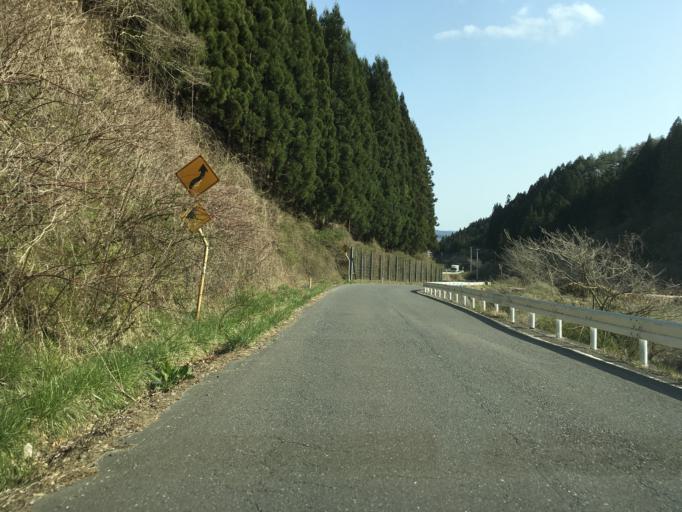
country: JP
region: Iwate
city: Ichinoseki
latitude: 38.8089
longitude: 141.3142
